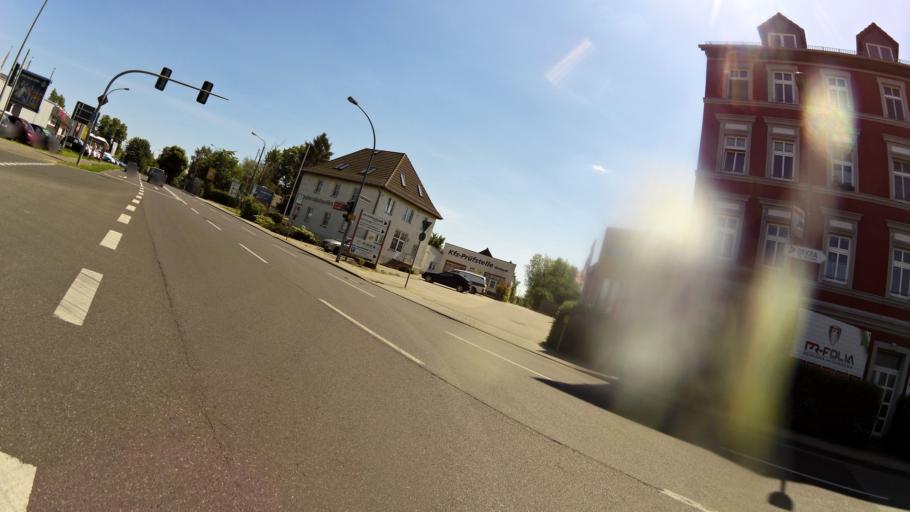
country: DE
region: Brandenburg
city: Frankfurt (Oder)
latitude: 52.3627
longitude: 14.5297
